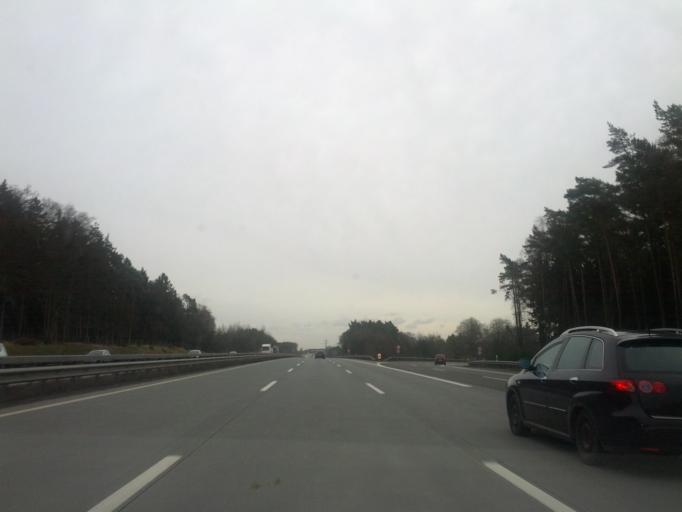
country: DE
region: Lower Saxony
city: Buchholz in der Nordheide
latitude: 53.3724
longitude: 9.8433
